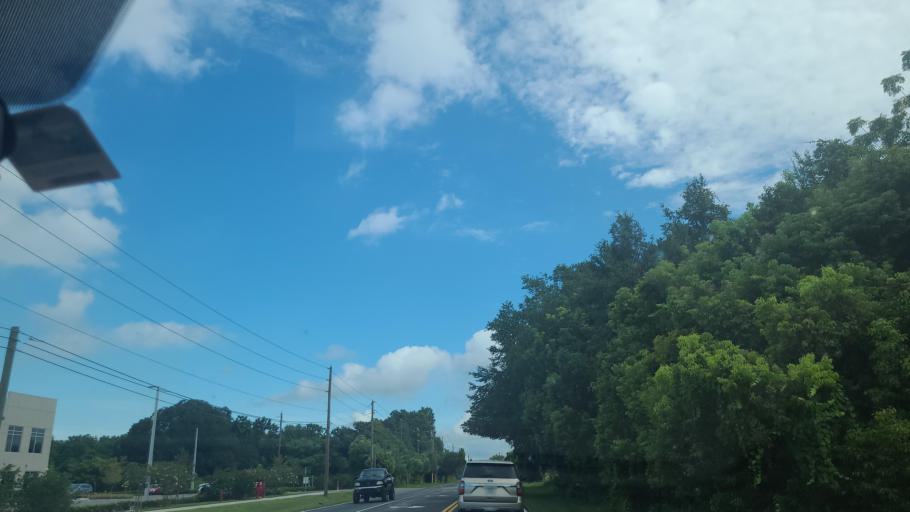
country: US
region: Florida
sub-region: Orange County
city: Ocoee
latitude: 28.5761
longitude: -81.5507
